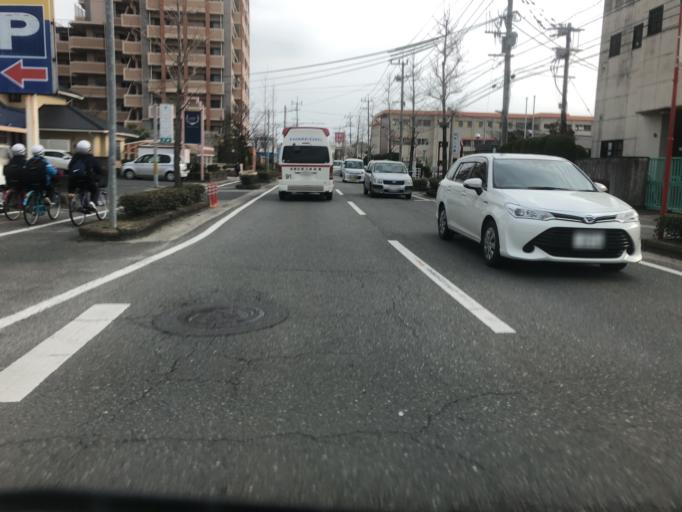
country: JP
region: Saga Prefecture
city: Saga-shi
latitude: 33.2756
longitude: 130.2706
